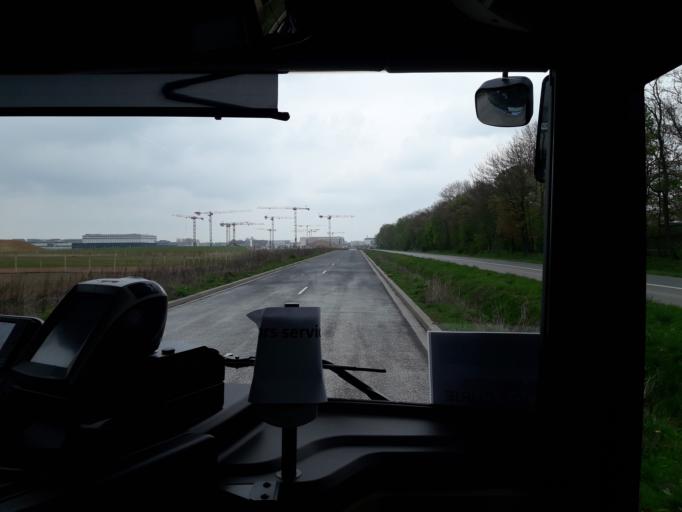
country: FR
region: Ile-de-France
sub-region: Departement de l'Essonne
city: Orsay
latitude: 48.7145
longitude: 2.1838
